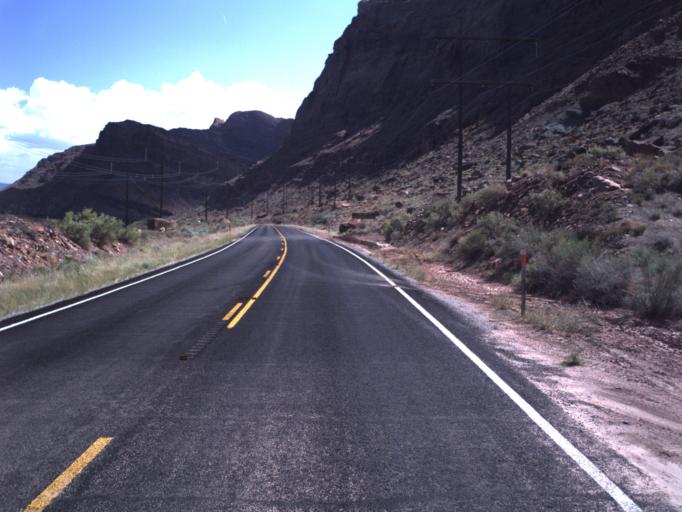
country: US
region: Utah
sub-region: Grand County
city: Moab
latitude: 38.5874
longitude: -109.5925
